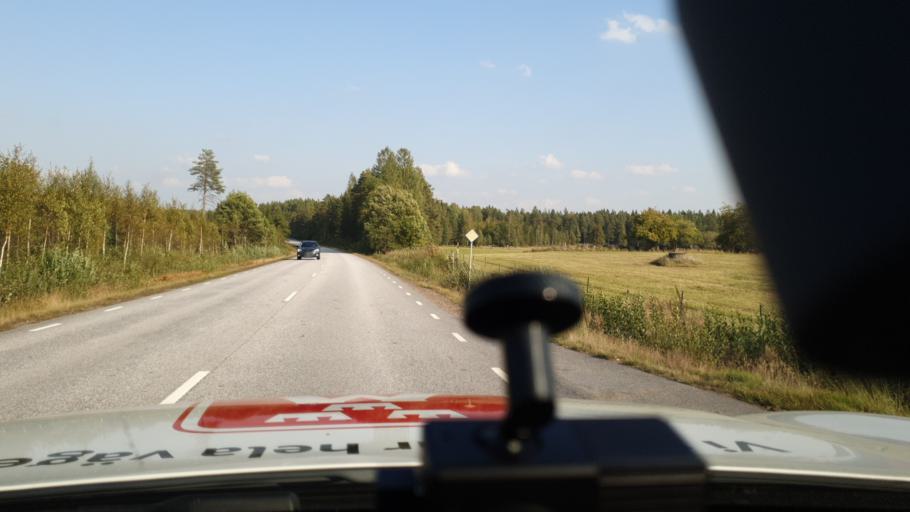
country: SE
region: Kalmar
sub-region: Vimmerby Kommun
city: Vimmerby
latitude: 57.5877
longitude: 15.9963
